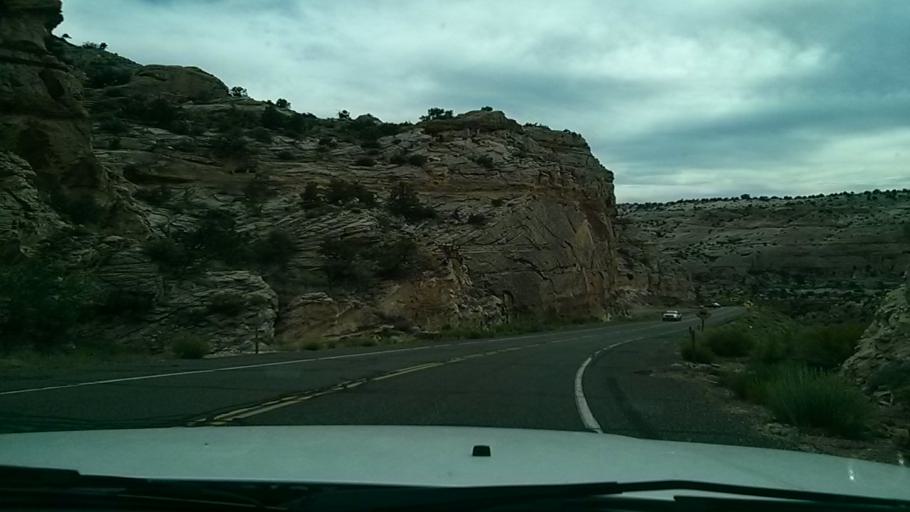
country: US
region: Utah
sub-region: Wayne County
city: Loa
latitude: 37.7983
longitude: -111.4079
